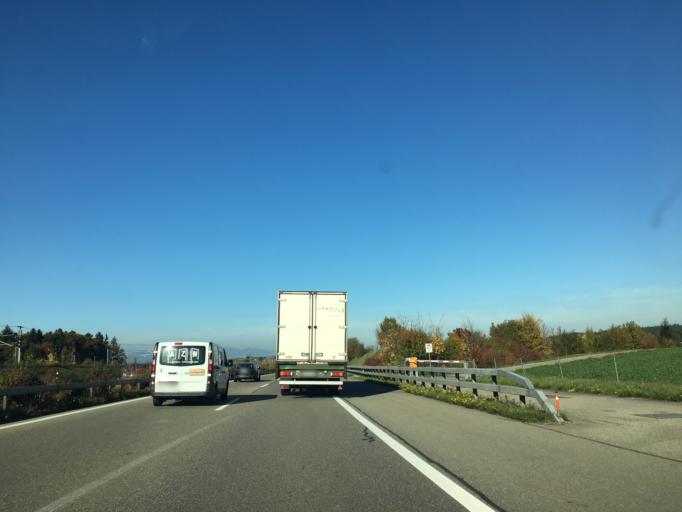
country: CH
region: Bern
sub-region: Emmental District
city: Hindelbank
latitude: 47.0458
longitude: 7.5306
